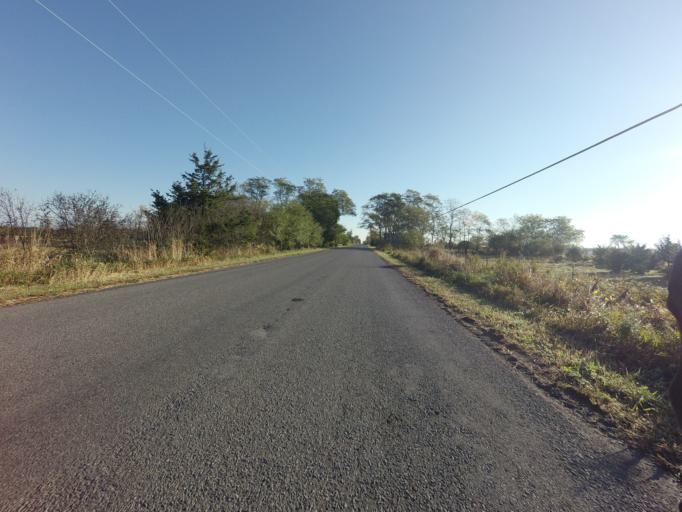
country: CA
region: Ontario
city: Belleville
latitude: 44.0569
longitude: -77.4091
